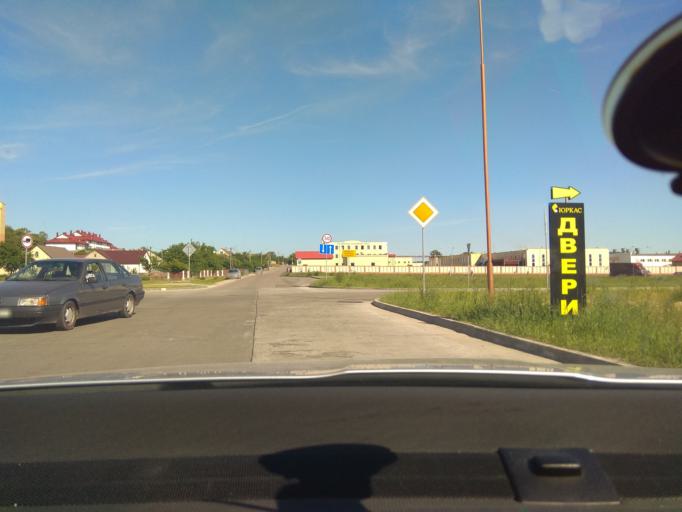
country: BY
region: Grodnenskaya
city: Hrodna
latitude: 53.6449
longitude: 23.7757
